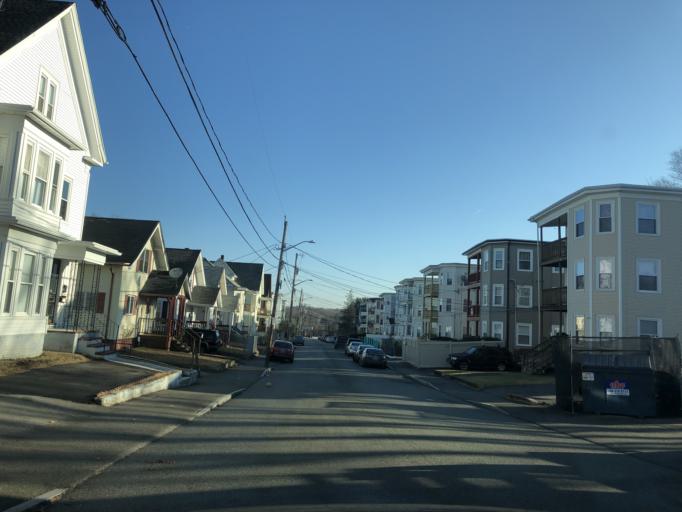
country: US
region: Massachusetts
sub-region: Plymouth County
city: Brockton
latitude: 42.1072
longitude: -71.0279
